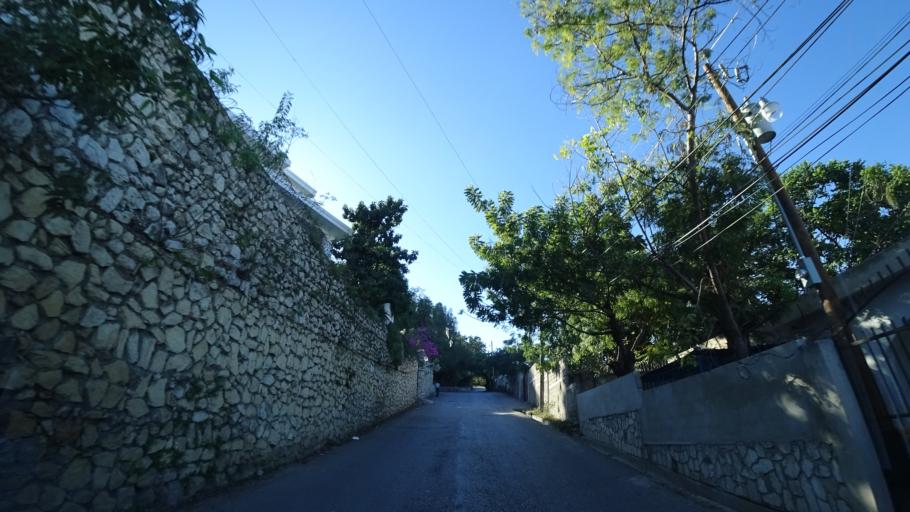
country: HT
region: Ouest
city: Petionville
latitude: 18.5073
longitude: -72.2934
